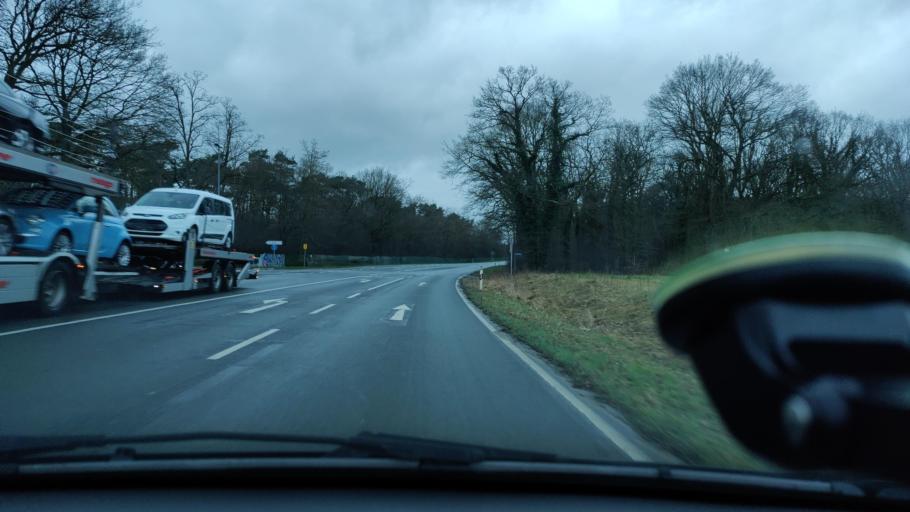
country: DE
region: North Rhine-Westphalia
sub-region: Regierungsbezirk Dusseldorf
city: Weeze
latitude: 51.5967
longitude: 6.1732
